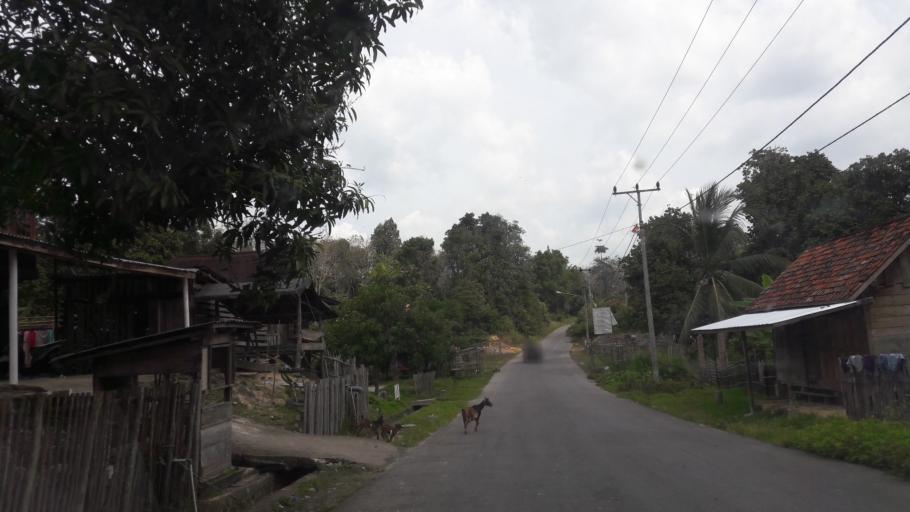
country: ID
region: South Sumatra
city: Gunungmenang
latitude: -3.1186
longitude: 103.8613
